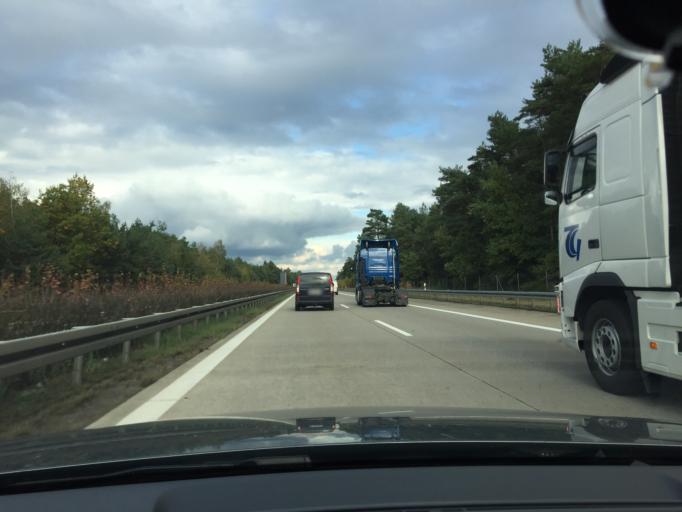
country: DE
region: Brandenburg
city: Ruhland
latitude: 51.4459
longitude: 13.8392
